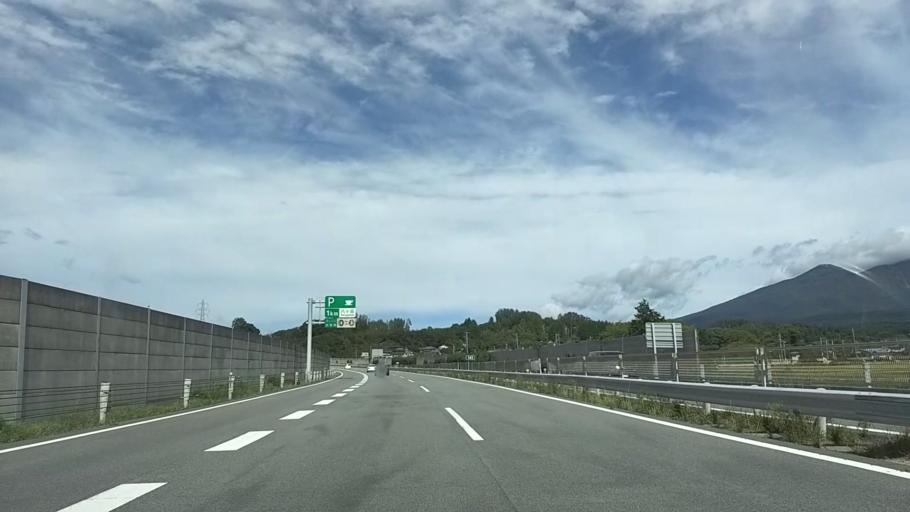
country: JP
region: Yamanashi
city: Nirasaki
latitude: 35.8415
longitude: 138.3819
